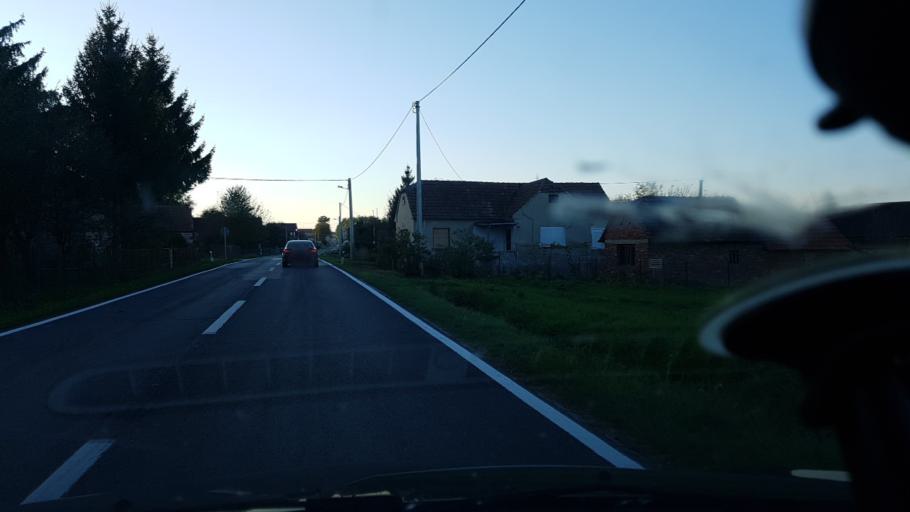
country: HR
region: Koprivnicko-Krizevacka
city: Hlebine
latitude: 46.1073
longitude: 16.9053
